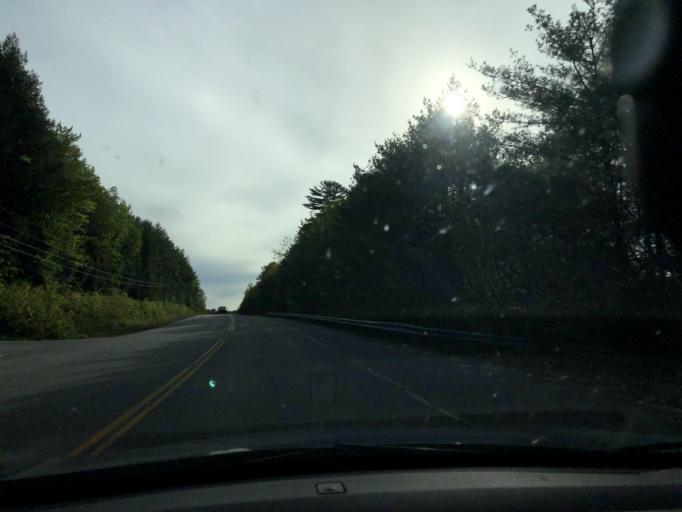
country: US
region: New Hampshire
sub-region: Merrimack County
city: Wilmot
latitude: 43.4173
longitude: -71.9330
